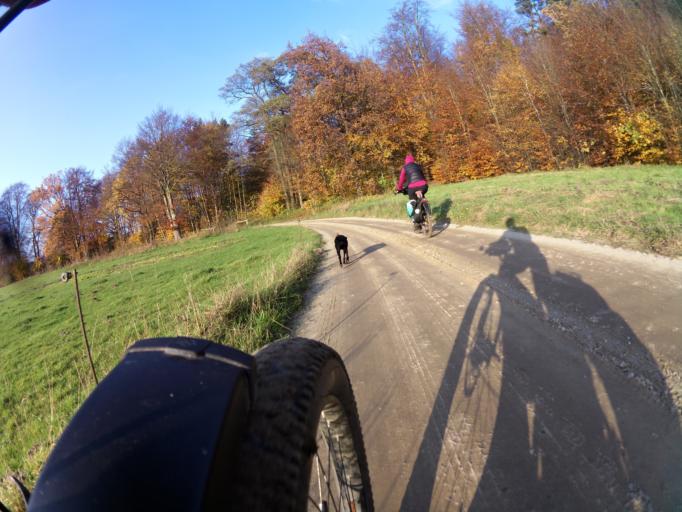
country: PL
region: Pomeranian Voivodeship
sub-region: Powiat pucki
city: Krokowa
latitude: 54.7493
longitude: 18.1962
